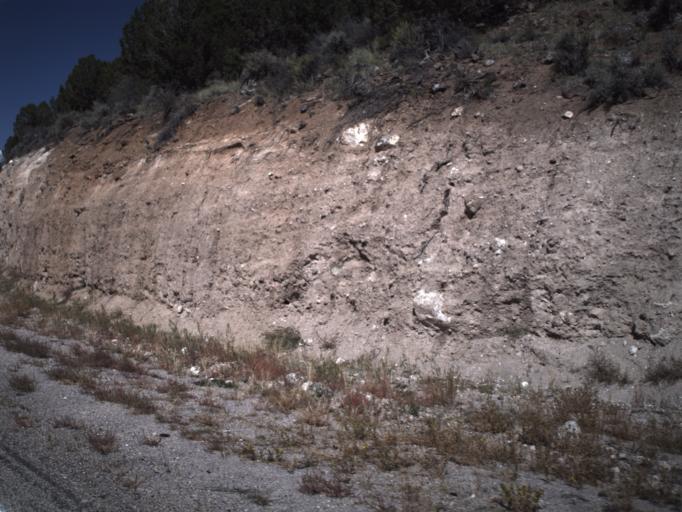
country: US
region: Utah
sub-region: Washington County
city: Enterprise
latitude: 37.5451
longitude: -113.6849
